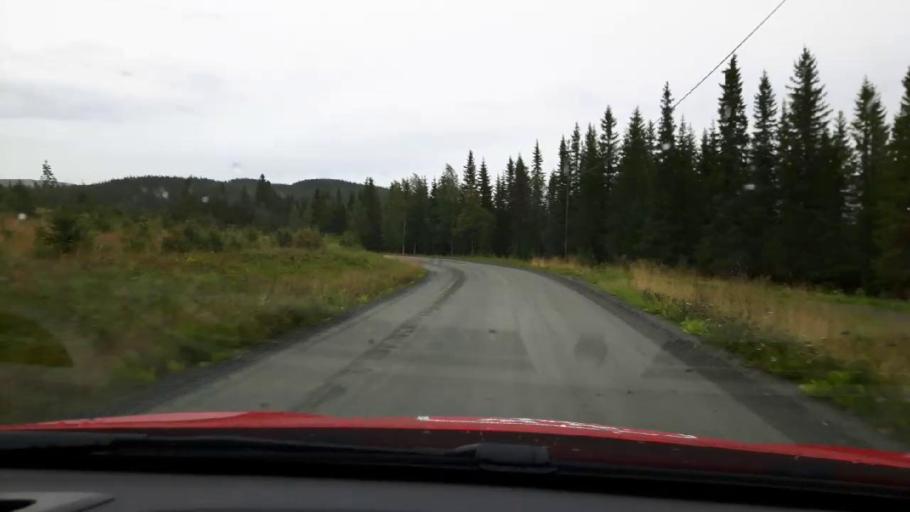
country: SE
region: Jaemtland
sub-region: Are Kommun
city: Are
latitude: 63.4264
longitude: 12.8088
